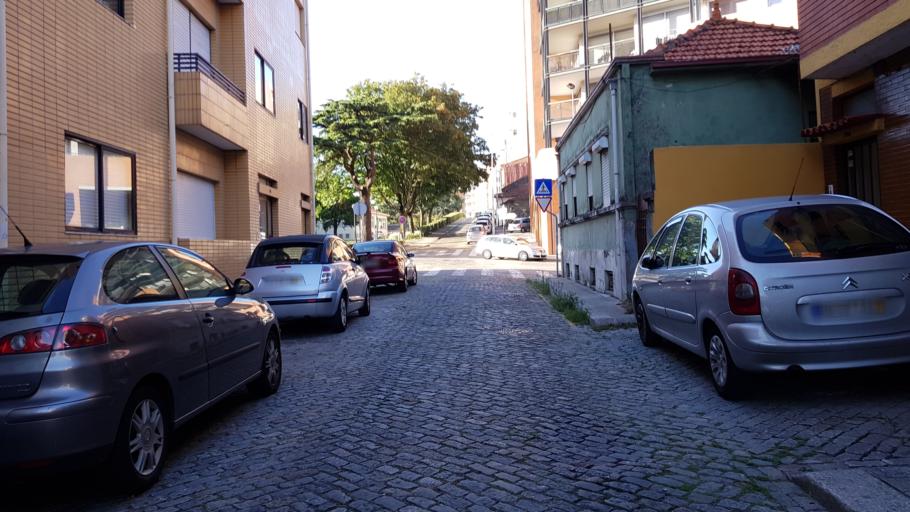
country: PT
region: Porto
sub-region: Porto
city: Porto
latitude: 41.1575
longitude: -8.5982
